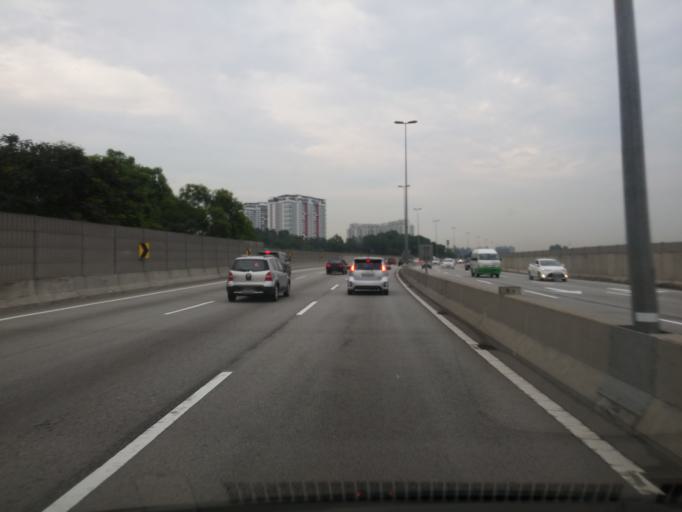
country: MY
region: Kuala Lumpur
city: Kuala Lumpur
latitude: 3.0691
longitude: 101.6852
